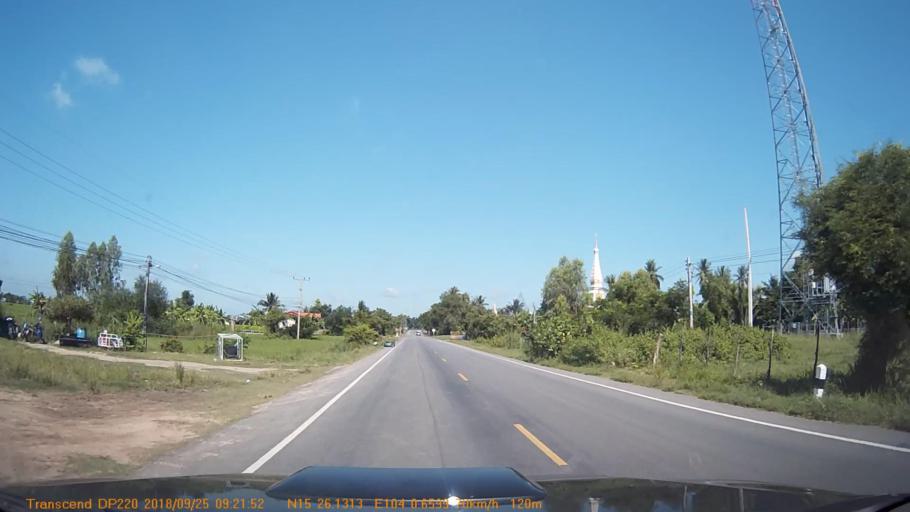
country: TH
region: Roi Et
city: Phon Sai
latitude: 15.4355
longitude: 104.0110
